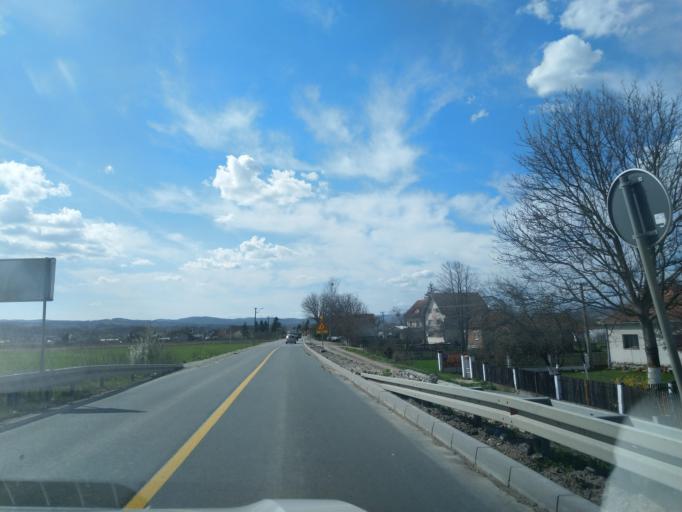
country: RS
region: Central Serbia
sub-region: Zlatiborski Okrug
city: Pozega
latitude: 43.8296
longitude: 20.0637
